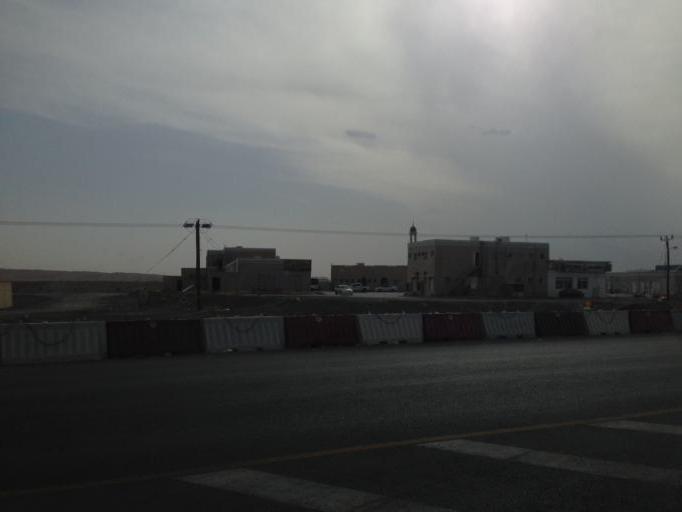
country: OM
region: Ash Sharqiyah
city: Al Qabil
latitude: 22.5324
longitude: 58.7327
